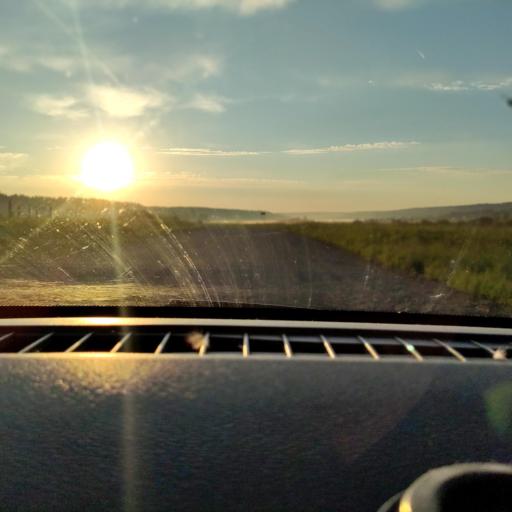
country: RU
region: Perm
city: Sylva
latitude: 57.8408
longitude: 56.6978
